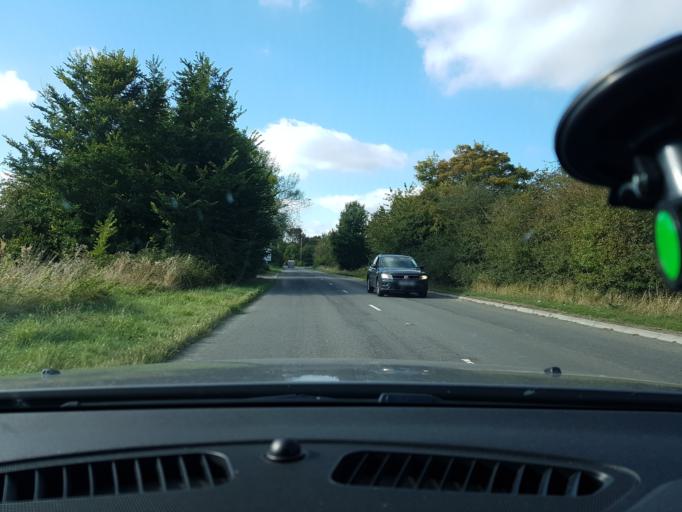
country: GB
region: England
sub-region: Borough of Swindon
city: Wanborough
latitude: 51.5388
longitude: -1.7184
